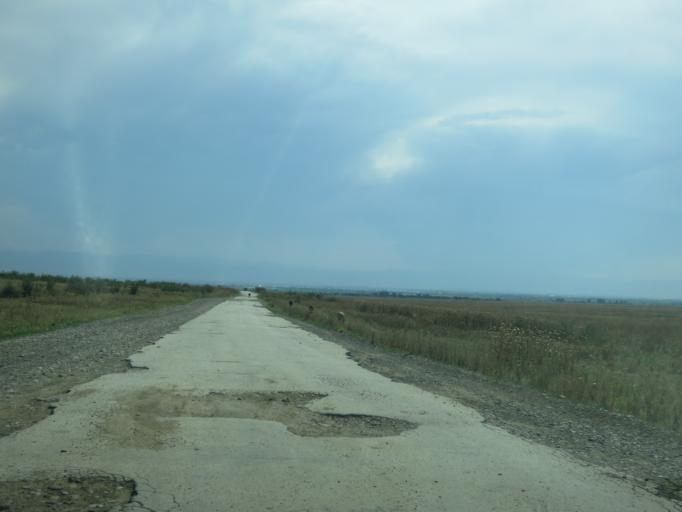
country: GE
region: Kvemo Kartli
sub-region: Gardabani
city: Gardabani
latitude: 41.4949
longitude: 45.1878
